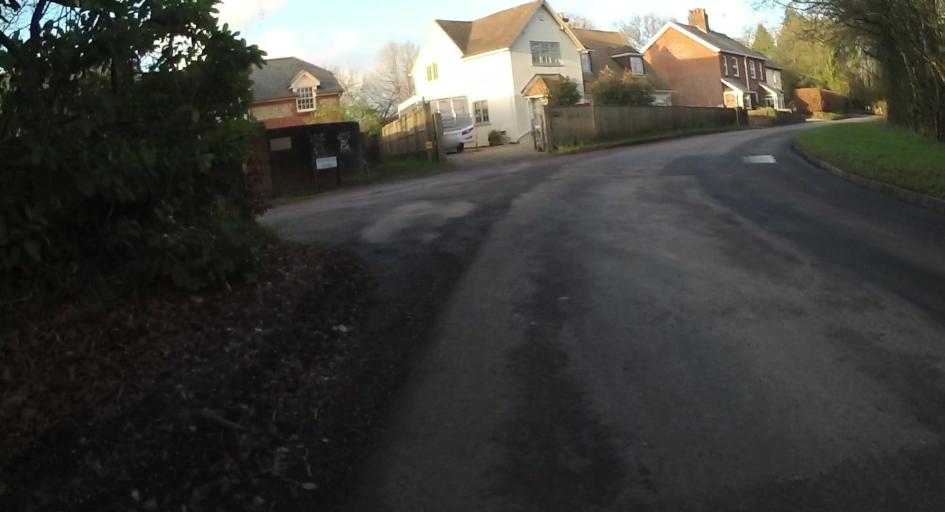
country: GB
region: England
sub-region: Hampshire
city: Four Marks
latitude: 51.1248
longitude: -1.0630
